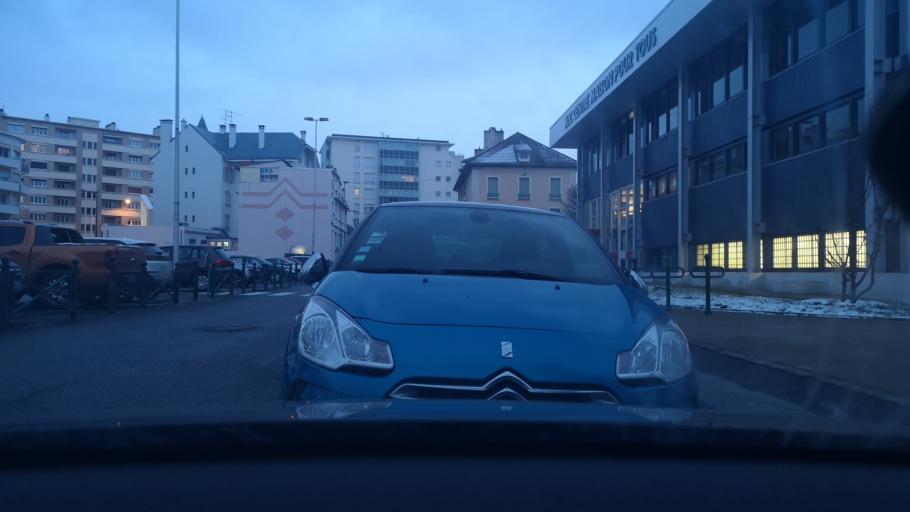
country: FR
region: Rhone-Alpes
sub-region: Departement de la Haute-Savoie
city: Annemasse
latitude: 46.1917
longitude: 6.2324
